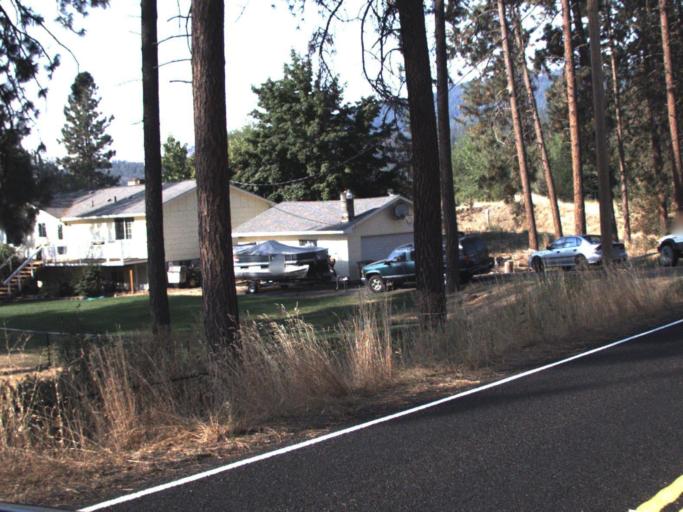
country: US
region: Washington
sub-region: Spokane County
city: Deer Park
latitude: 47.8921
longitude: -117.6787
